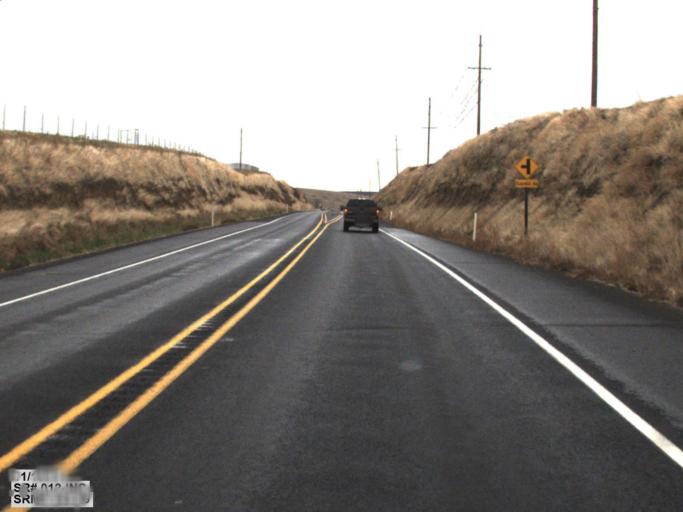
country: US
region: Washington
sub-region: Walla Walla County
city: Walla Walla East
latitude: 46.1049
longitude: -118.2376
